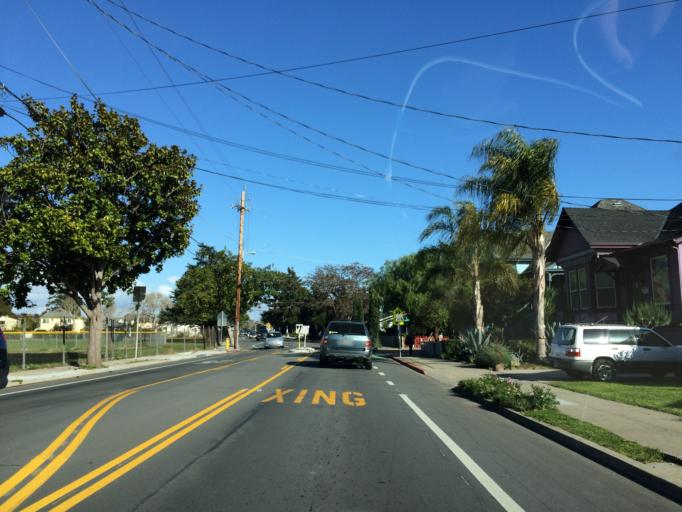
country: US
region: California
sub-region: Santa Cruz County
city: Santa Cruz
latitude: 36.9684
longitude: -122.0331
